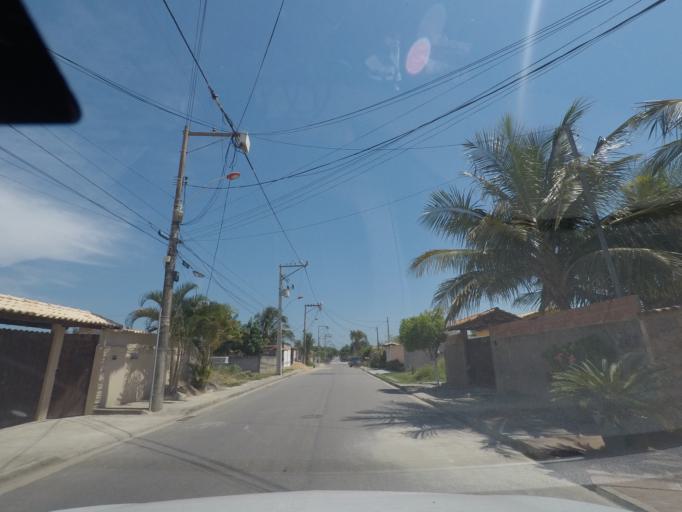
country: BR
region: Rio de Janeiro
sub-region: Marica
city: Marica
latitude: -22.9608
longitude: -42.9568
